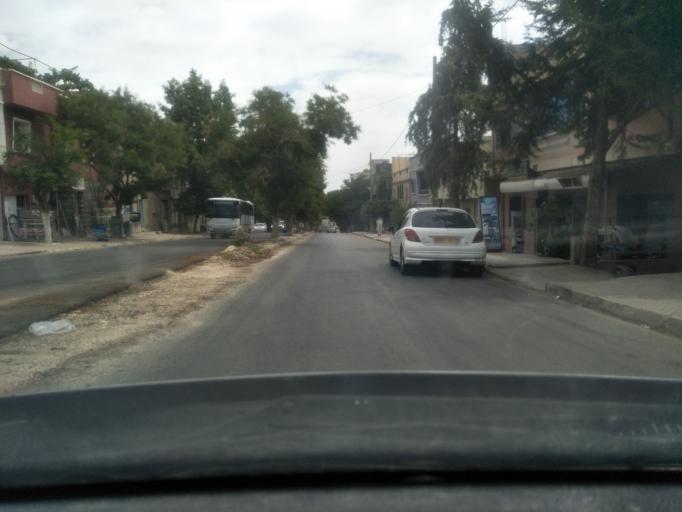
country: DZ
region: Tlemcen
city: Tlemcen
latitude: 34.9039
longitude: -1.3242
